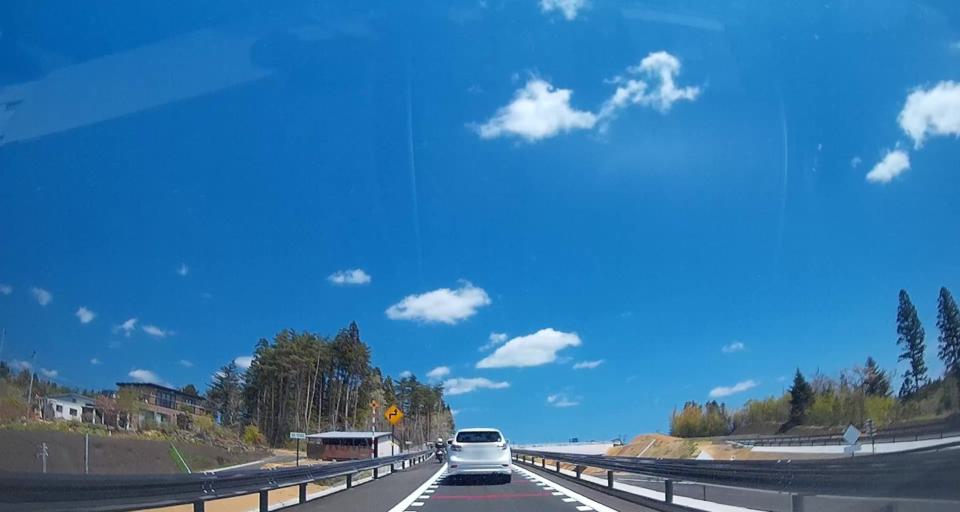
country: JP
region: Miyagi
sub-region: Oshika Gun
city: Onagawa Cho
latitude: 38.7792
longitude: 141.5086
